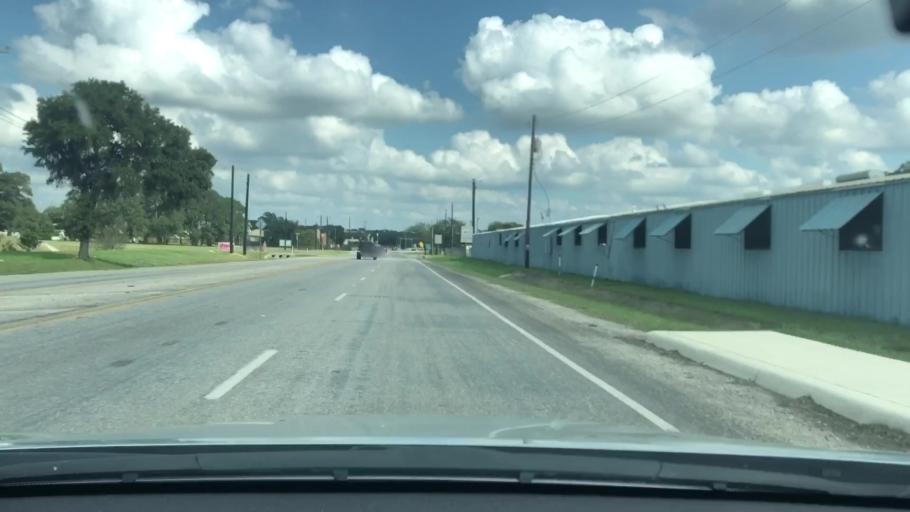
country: US
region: Texas
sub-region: Kendall County
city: Boerne
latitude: 29.7891
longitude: -98.7101
